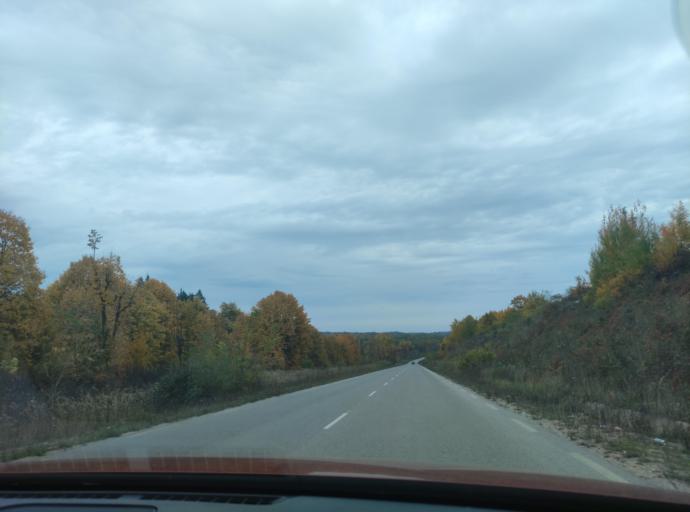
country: BG
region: Montana
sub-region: Obshtina Berkovitsa
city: Berkovitsa
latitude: 43.2299
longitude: 23.1580
